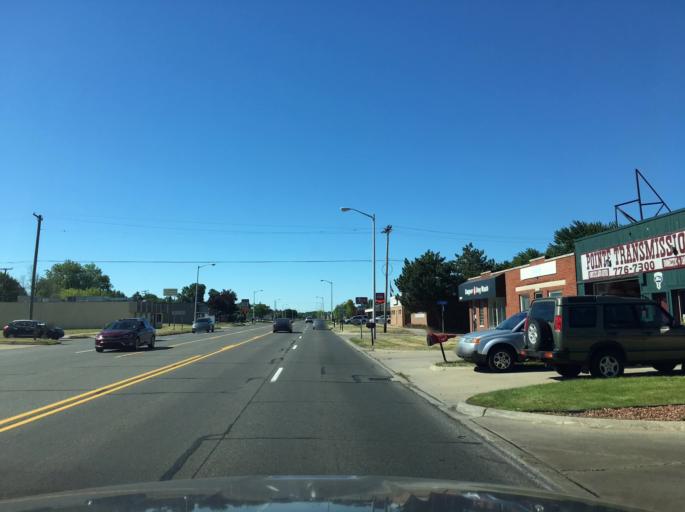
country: US
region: Michigan
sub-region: Macomb County
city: Saint Clair Shores
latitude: 42.5024
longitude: -82.8980
